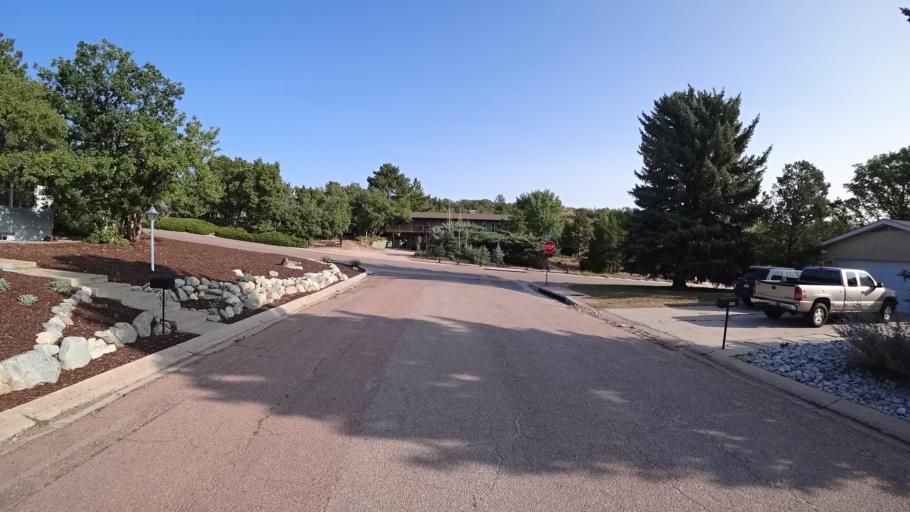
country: US
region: Colorado
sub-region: El Paso County
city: Colorado Springs
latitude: 38.8214
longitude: -104.8677
